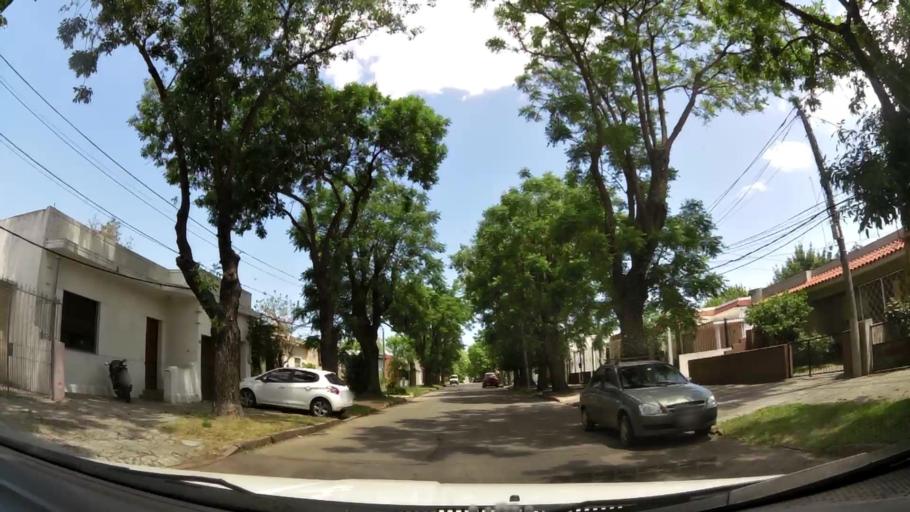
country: UY
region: Montevideo
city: Montevideo
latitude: -34.8652
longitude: -56.1889
